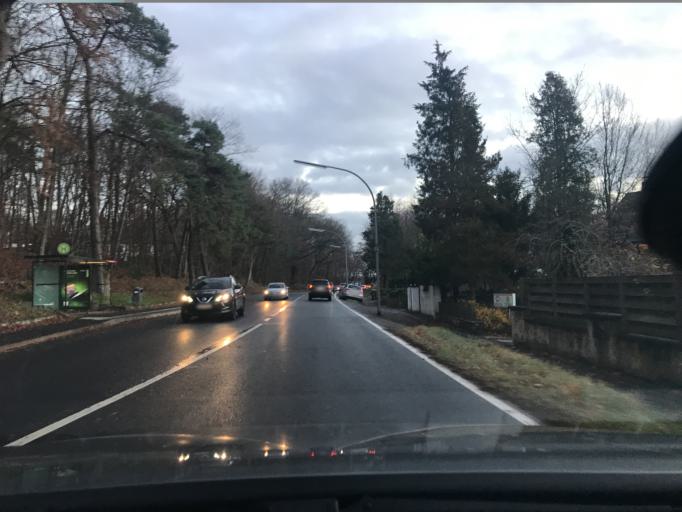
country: DE
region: North Rhine-Westphalia
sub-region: Regierungsbezirk Koln
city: Merheim
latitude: 50.9525
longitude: 7.0780
